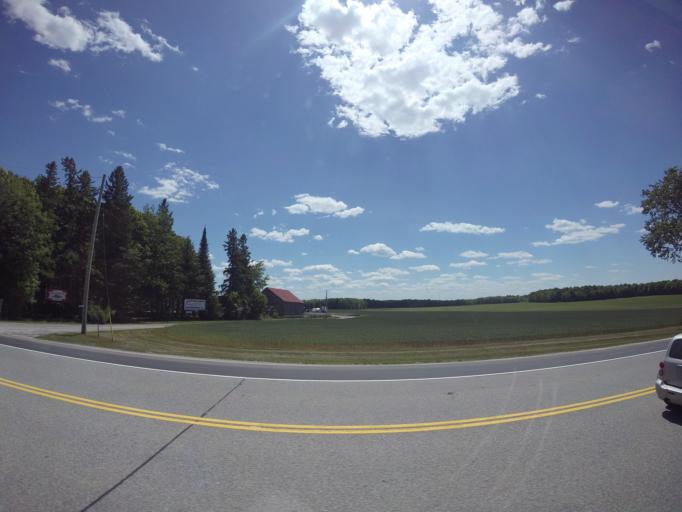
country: CA
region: Ontario
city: Carleton Place
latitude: 45.1328
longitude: -76.1929
